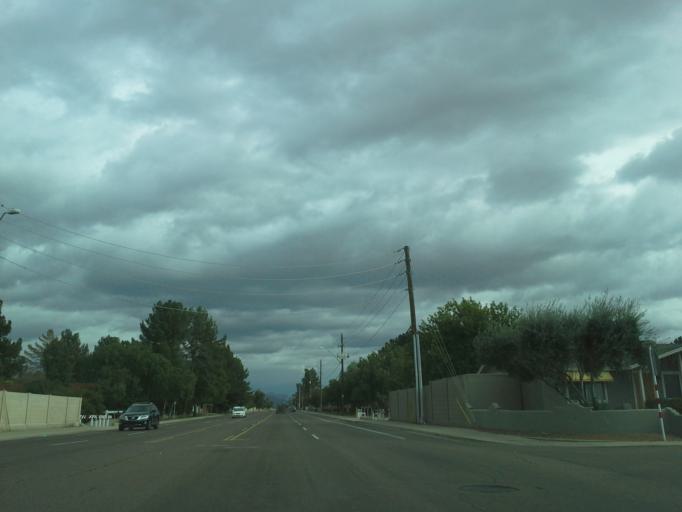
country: US
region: Arizona
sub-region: Maricopa County
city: Paradise Valley
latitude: 33.6118
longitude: -111.9926
